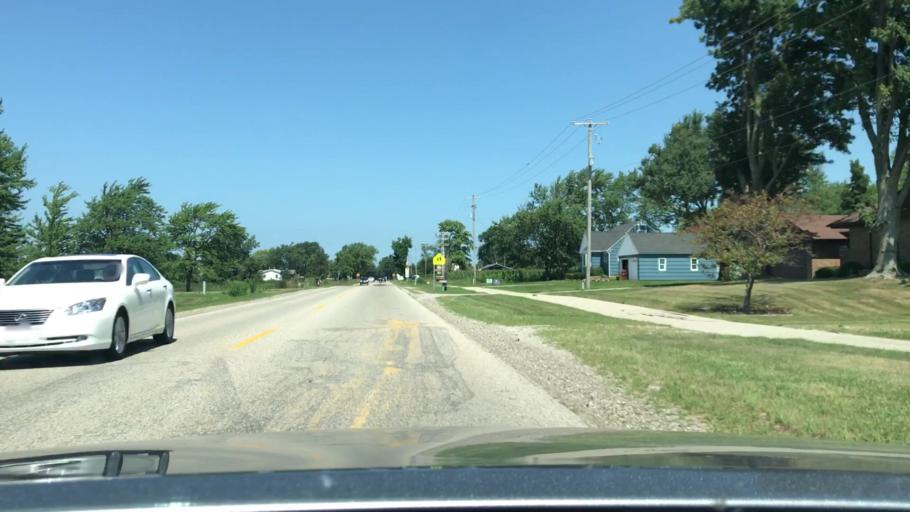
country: US
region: Michigan
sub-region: Ottawa County
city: Holland
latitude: 42.8514
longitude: -86.0791
